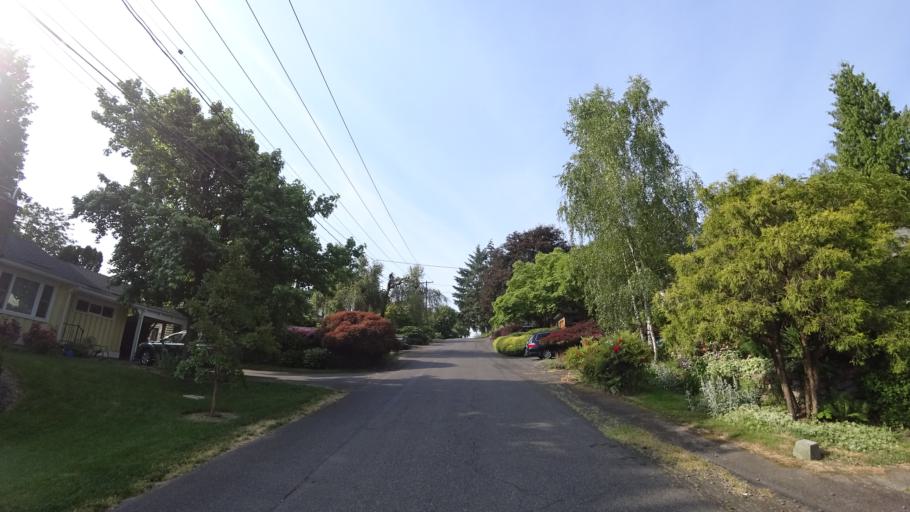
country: US
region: Oregon
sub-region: Washington County
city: Garden Home-Whitford
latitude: 45.4598
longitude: -122.7135
